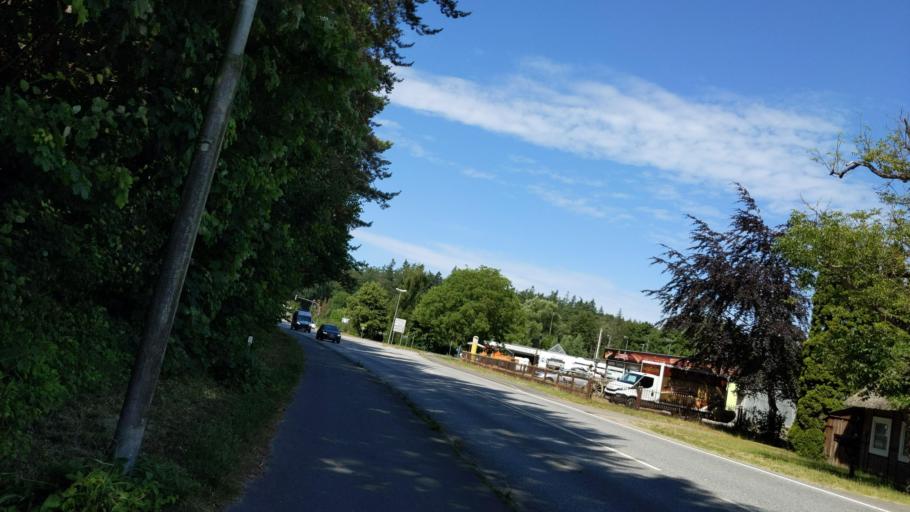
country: DE
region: Schleswig-Holstein
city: Bosdorf
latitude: 54.1458
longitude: 10.4591
